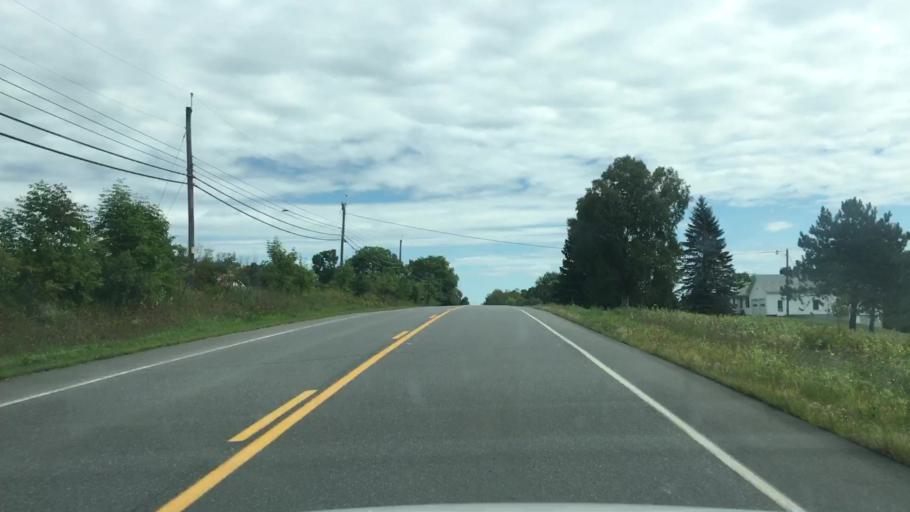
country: US
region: Maine
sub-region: Piscataquis County
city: Brownville
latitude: 45.2277
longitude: -69.1085
